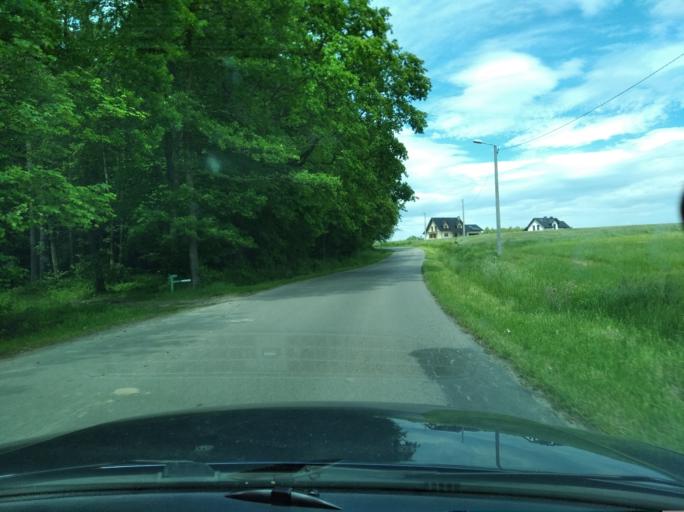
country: PL
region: Subcarpathian Voivodeship
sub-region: Powiat ropczycko-sedziszowski
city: Ropczyce
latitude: 50.0056
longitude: 21.6140
